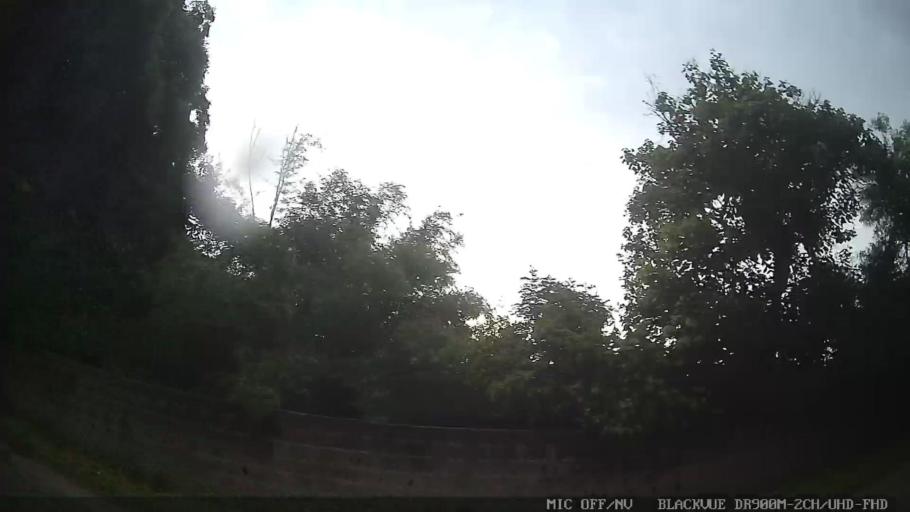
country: BR
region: Sao Paulo
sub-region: Ribeirao Pires
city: Ribeirao Pires
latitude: -23.6830
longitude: -46.3597
